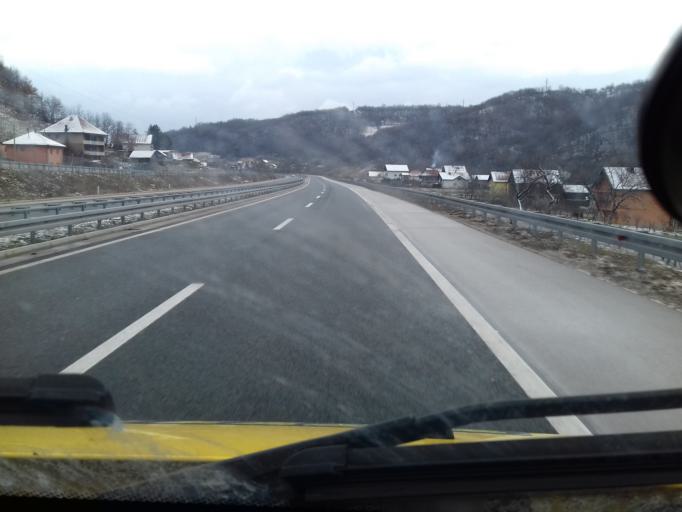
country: BA
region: Federation of Bosnia and Herzegovina
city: Kakanj
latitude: 44.1327
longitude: 18.0561
